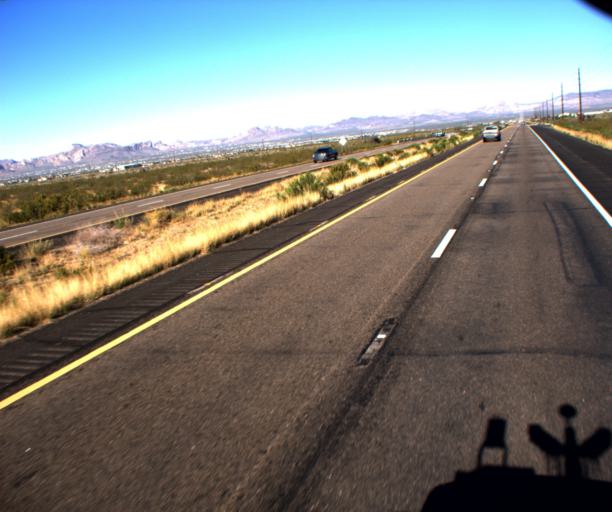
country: US
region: Arizona
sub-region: Mohave County
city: Golden Valley
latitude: 35.2226
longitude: -114.2240
